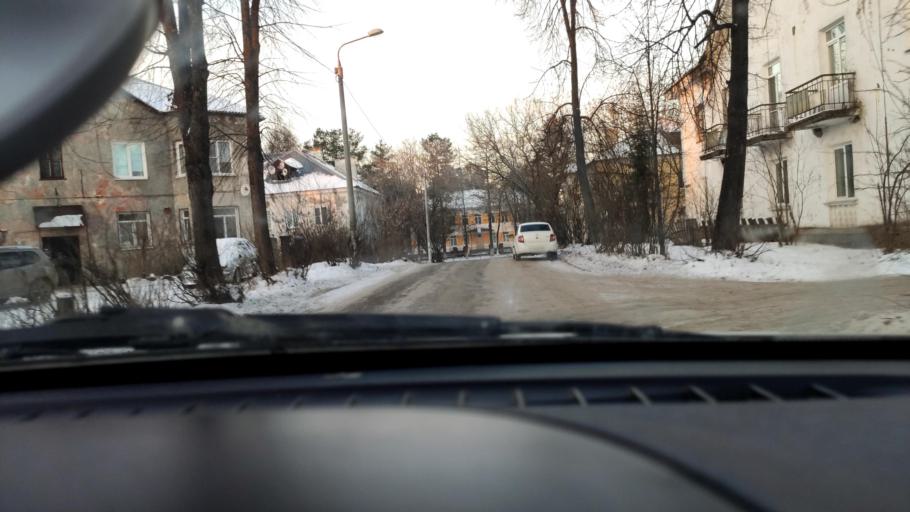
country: RU
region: Perm
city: Perm
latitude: 58.1129
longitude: 56.3160
